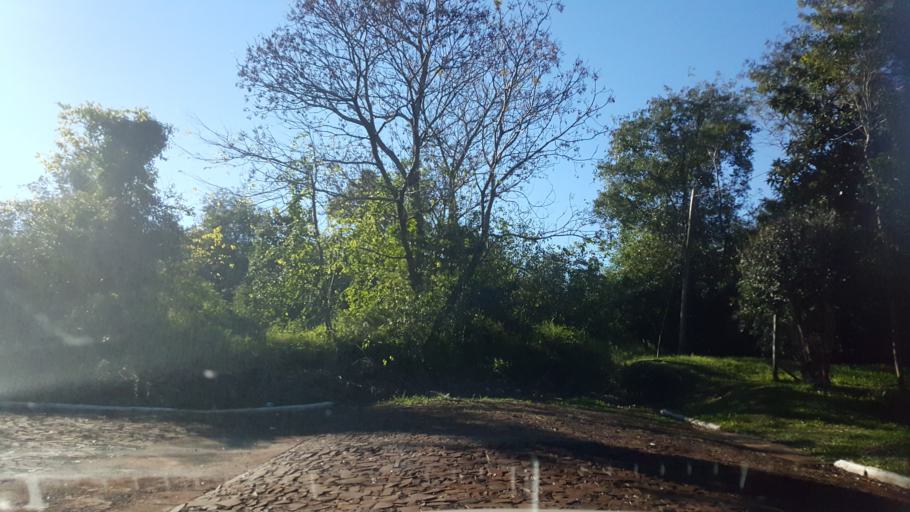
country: AR
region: Misiones
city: Jardin America
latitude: -27.0869
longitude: -55.2857
